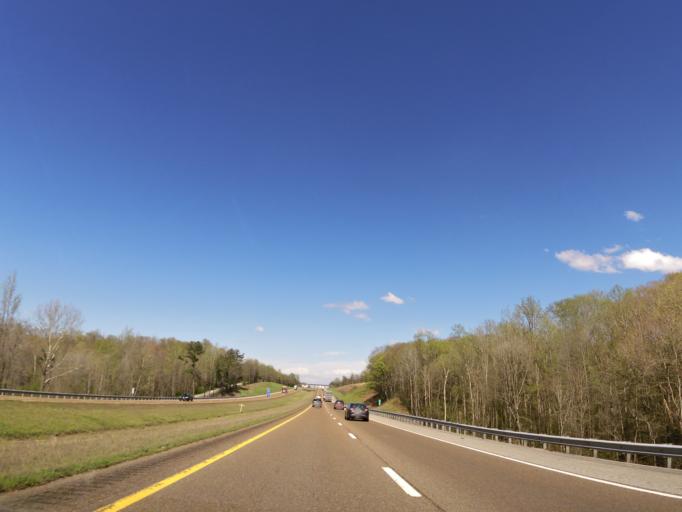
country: US
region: Tennessee
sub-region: Gibson County
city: Medina
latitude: 35.7319
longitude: -88.5931
